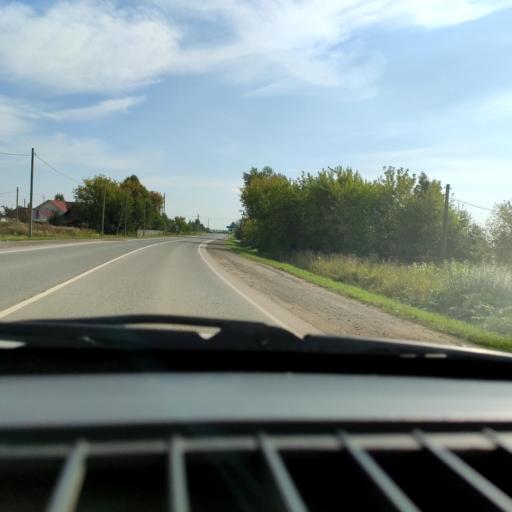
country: RU
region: Perm
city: Ust'-Kachka
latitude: 57.9924
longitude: 55.7139
